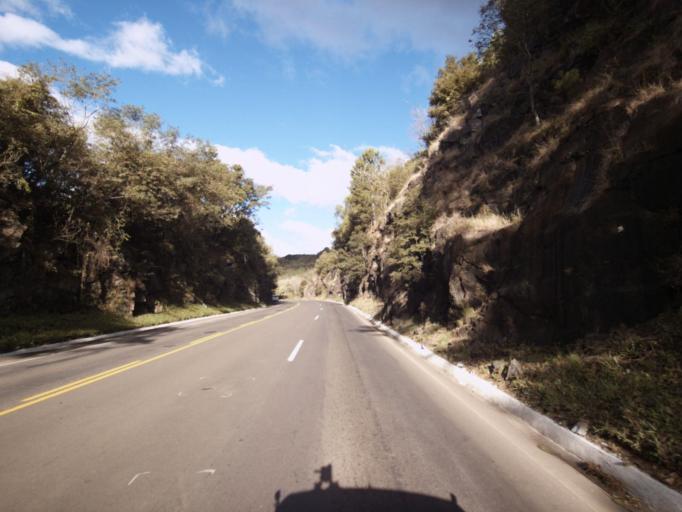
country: BR
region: Santa Catarina
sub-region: Joacaba
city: Joacaba
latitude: -27.2947
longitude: -51.4098
